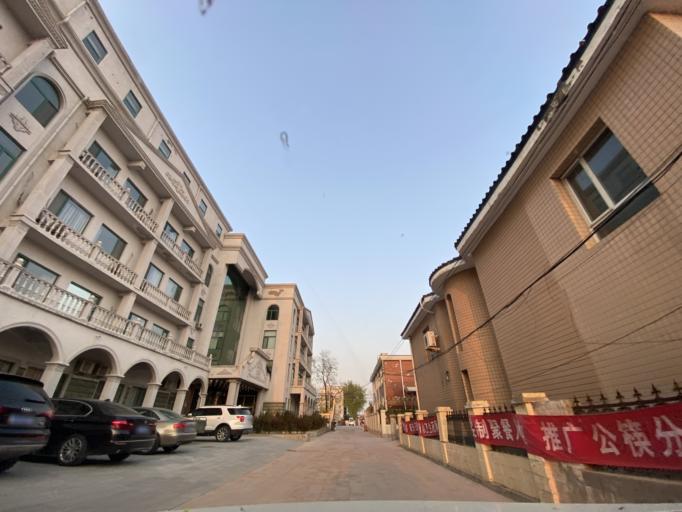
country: CN
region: Beijing
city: Weishanzhuang
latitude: 39.6093
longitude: 116.4209
